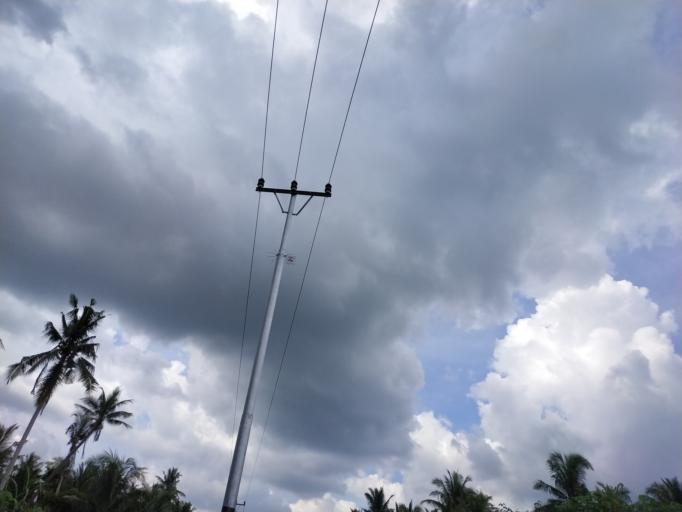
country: ID
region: Riau
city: Tembilahan
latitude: -0.2045
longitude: 103.2000
